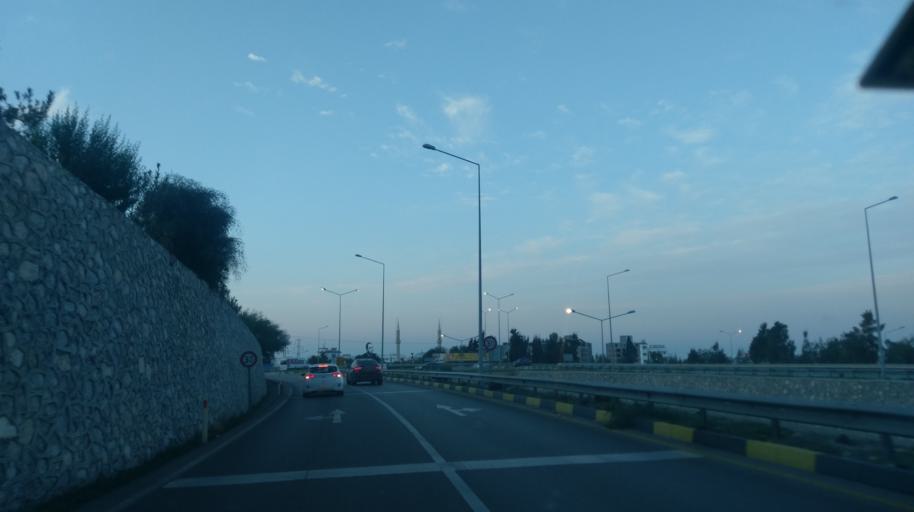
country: CY
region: Keryneia
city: Kyrenia
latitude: 35.3241
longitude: 33.3176
